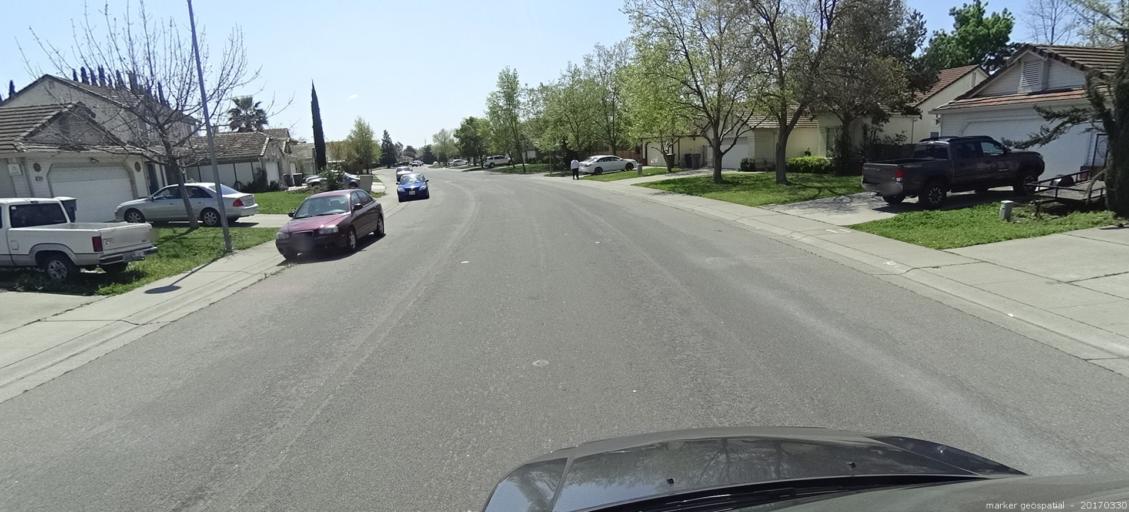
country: US
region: California
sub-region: Sacramento County
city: Florin
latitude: 38.4615
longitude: -121.4216
